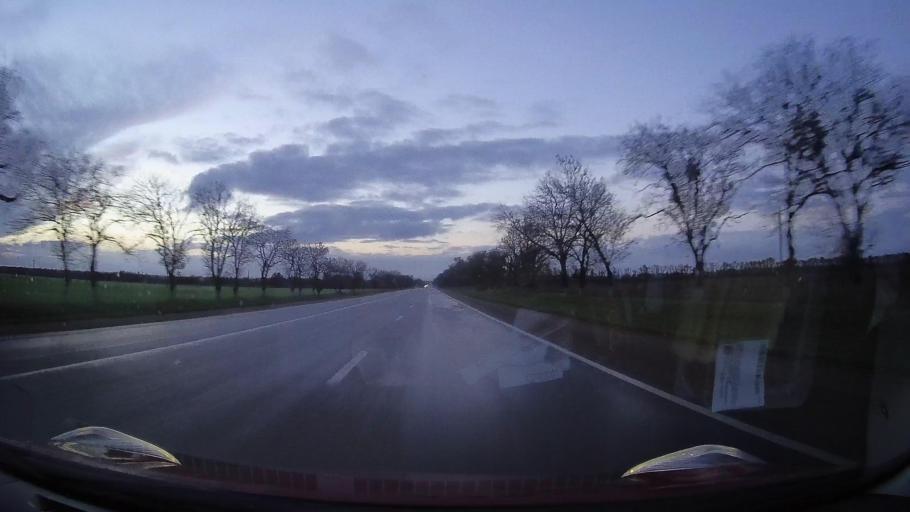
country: RU
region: Krasnodarskiy
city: Zavetnyy
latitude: 44.8946
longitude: 41.1978
